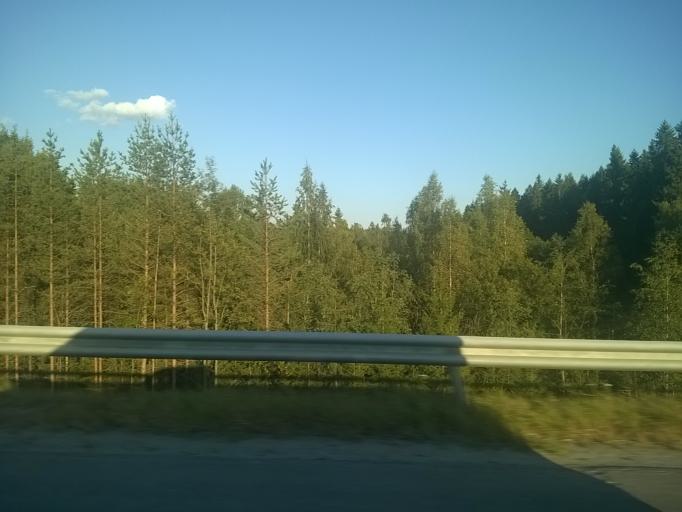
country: FI
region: Pirkanmaa
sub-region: Tampere
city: Tampere
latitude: 61.4382
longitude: 23.7591
